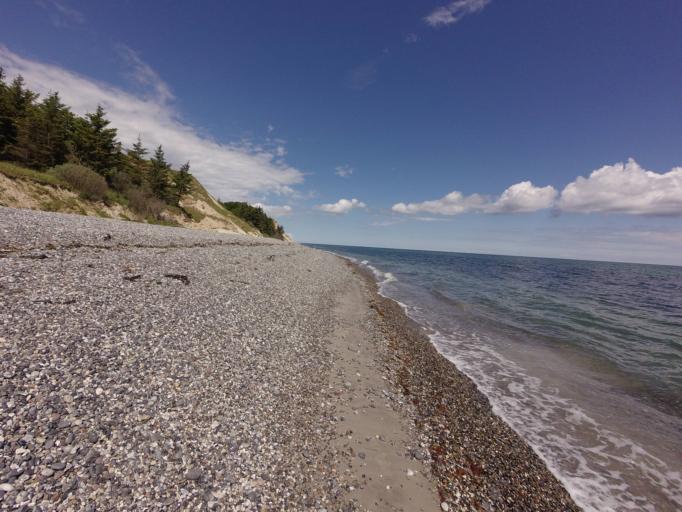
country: DK
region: Central Jutland
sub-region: Norddjurs Kommune
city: Grenaa
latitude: 56.5098
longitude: 10.8672
